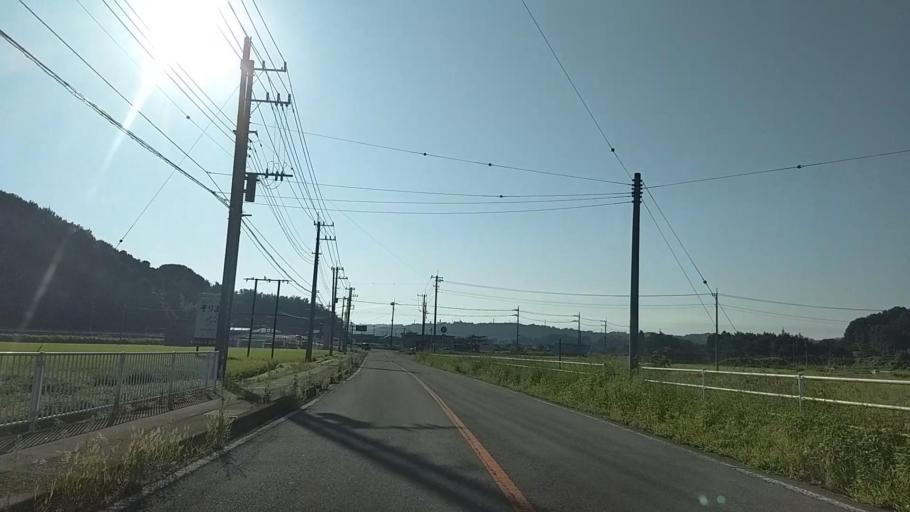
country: JP
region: Gunma
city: Annaka
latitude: 36.3419
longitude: 138.8860
